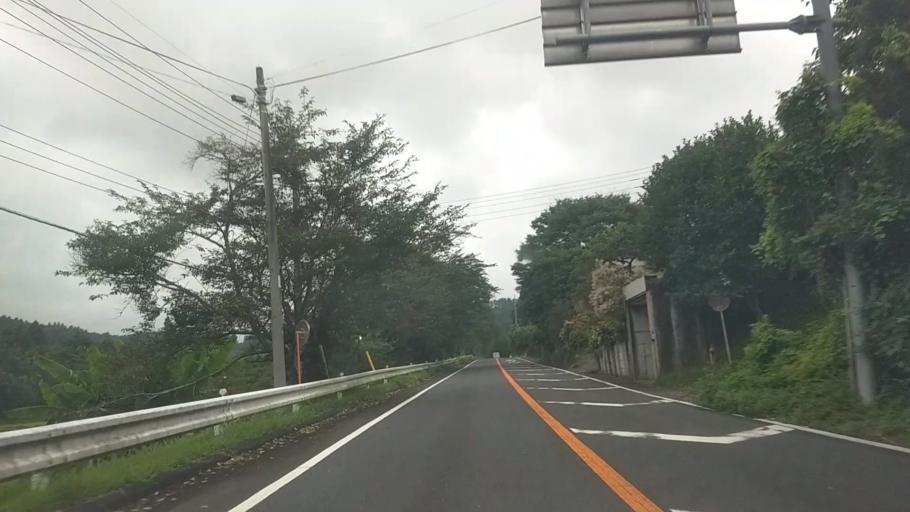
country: JP
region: Chiba
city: Kawaguchi
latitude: 35.2391
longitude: 140.0757
